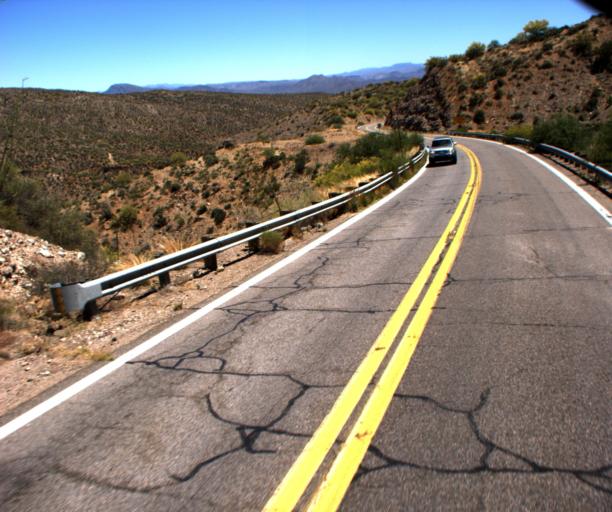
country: US
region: Arizona
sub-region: Pinal County
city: Kearny
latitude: 33.1703
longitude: -110.8078
